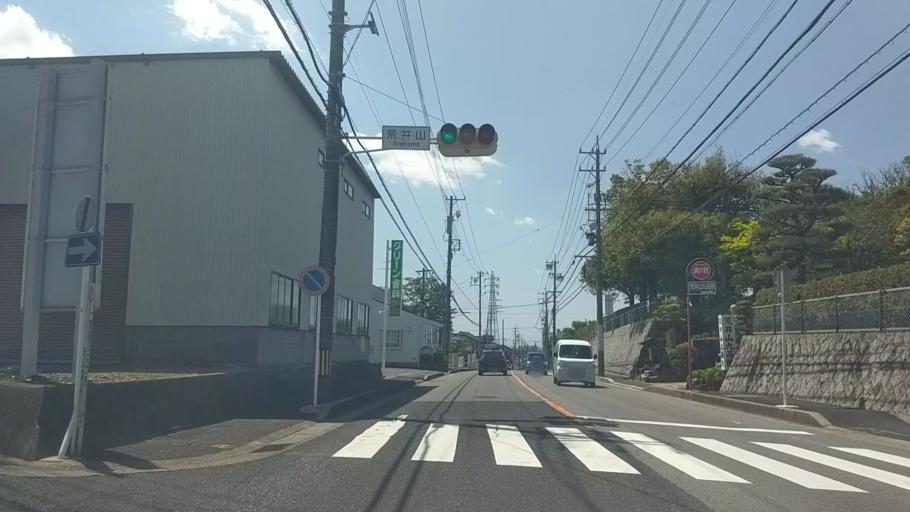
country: JP
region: Aichi
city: Okazaki
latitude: 34.9819
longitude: 137.1757
